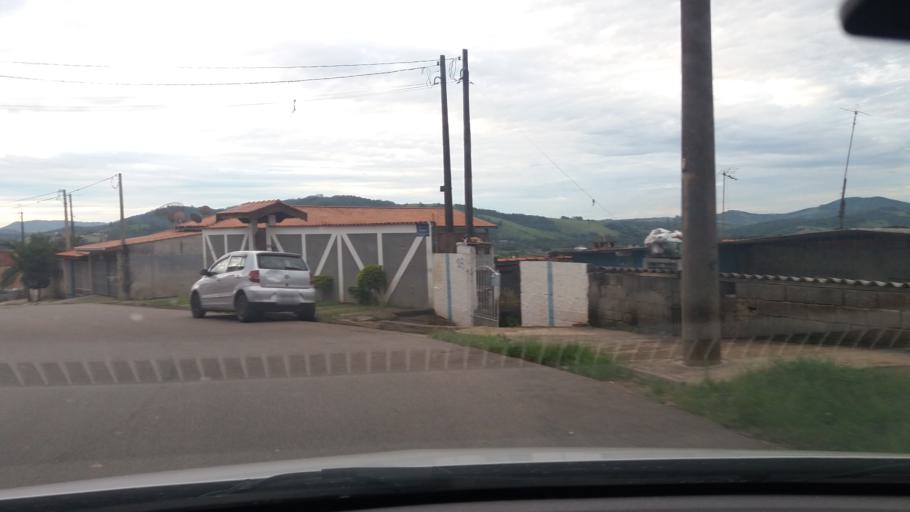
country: BR
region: Sao Paulo
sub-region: Bom Jesus Dos Perdoes
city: Bom Jesus dos Perdoes
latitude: -23.1241
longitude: -46.4730
